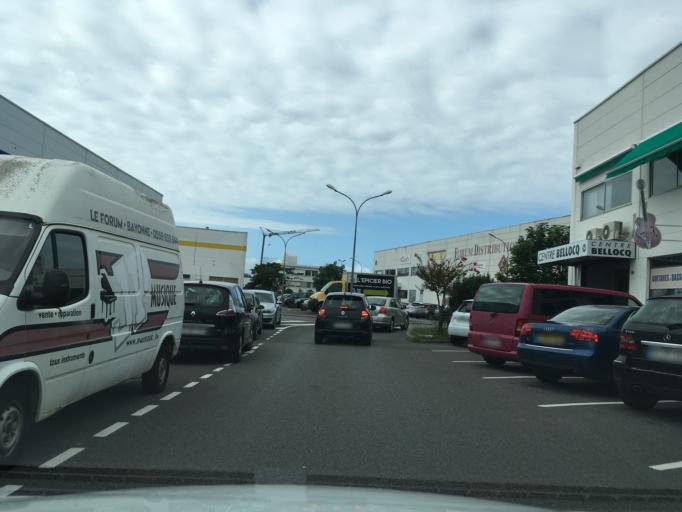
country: FR
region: Aquitaine
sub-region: Departement des Pyrenees-Atlantiques
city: Bayonne
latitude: 43.4908
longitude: -1.4923
